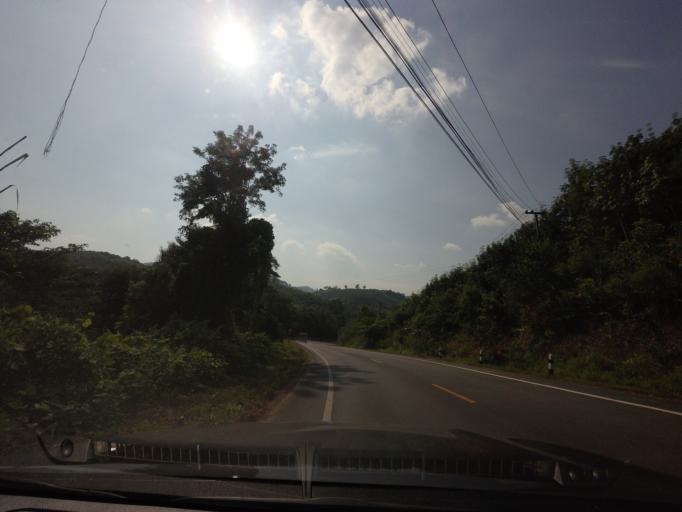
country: TH
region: Nan
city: Santi Suk
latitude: 18.9250
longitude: 100.9062
